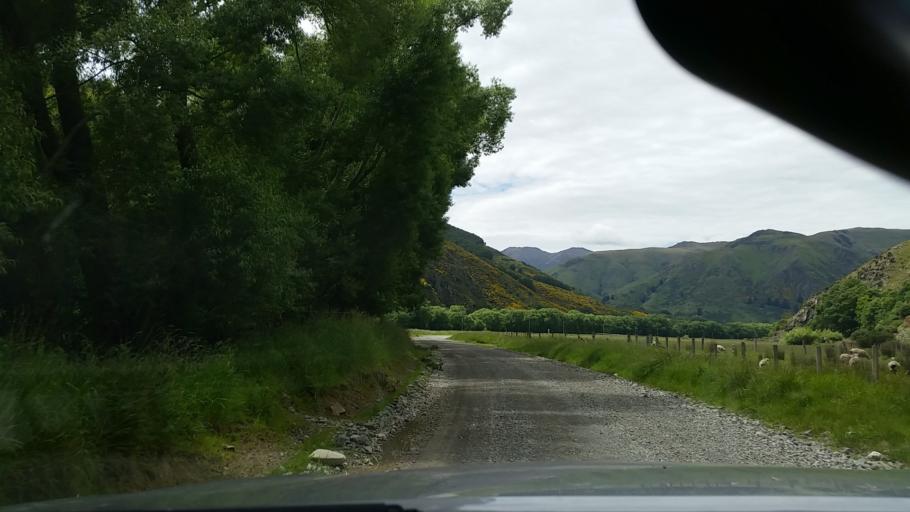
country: NZ
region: Otago
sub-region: Queenstown-Lakes District
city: Kingston
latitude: -45.5551
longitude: 168.6183
